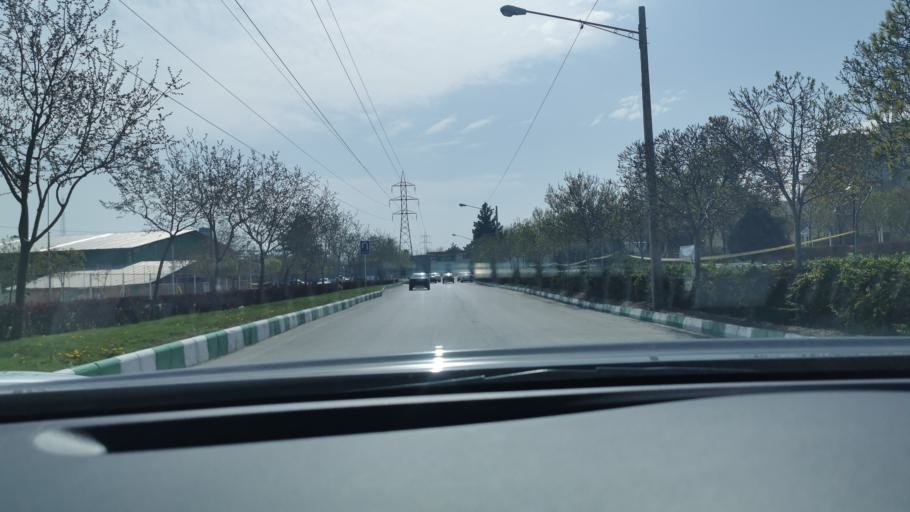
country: IR
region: Razavi Khorasan
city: Mashhad
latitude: 36.2810
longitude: 59.5480
